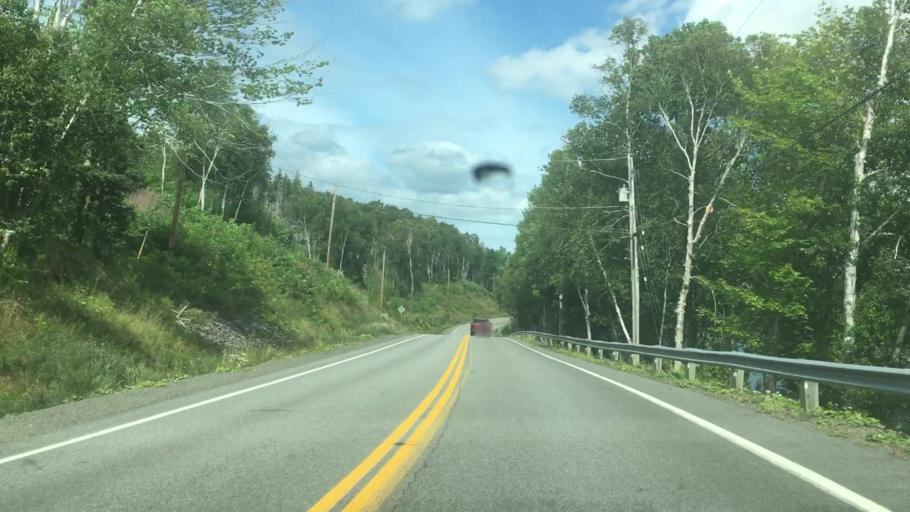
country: CA
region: Nova Scotia
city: Sydney Mines
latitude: 46.2683
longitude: -60.6086
